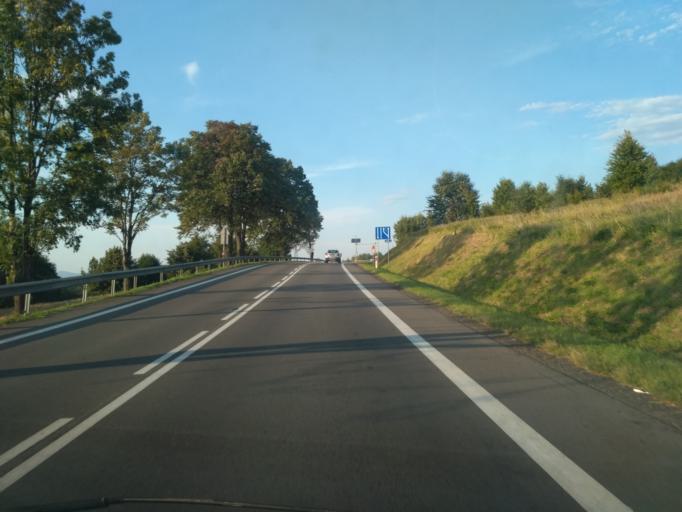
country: PL
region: Subcarpathian Voivodeship
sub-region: Powiat krosnienski
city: Dukla
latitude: 49.6026
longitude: 21.7253
